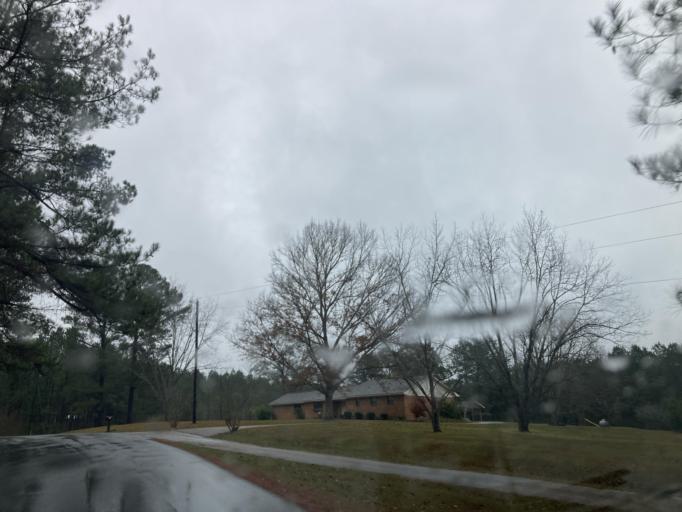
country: US
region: Mississippi
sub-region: Forrest County
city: Rawls Springs
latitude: 31.4641
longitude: -89.3824
